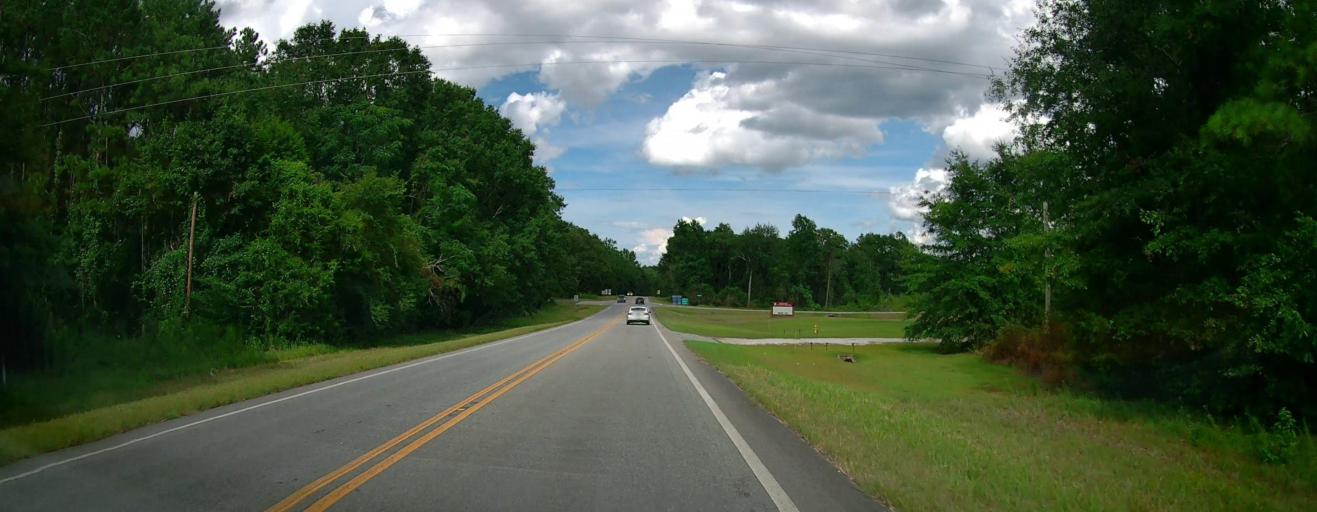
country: US
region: Alabama
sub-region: Russell County
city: Ladonia
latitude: 32.4424
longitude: -85.2942
